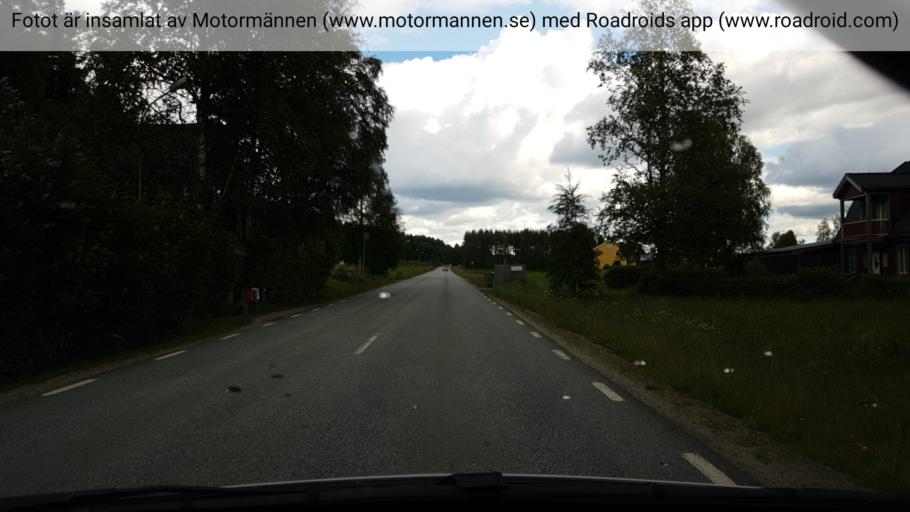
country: SE
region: Vaesterbotten
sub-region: Bjurholms Kommun
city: Bjurholm
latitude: 64.2415
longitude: 19.3306
